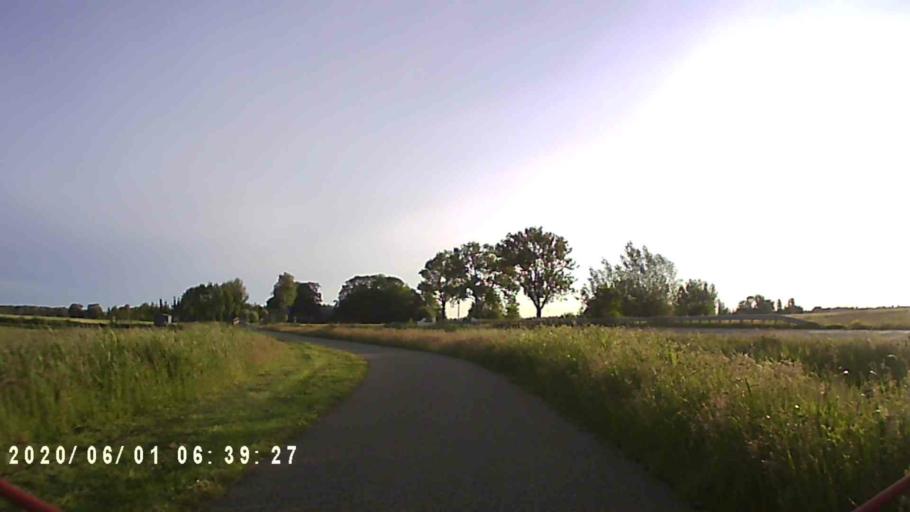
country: NL
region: Friesland
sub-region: Gemeente Kollumerland en Nieuwkruisland
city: Kollum
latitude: 53.2902
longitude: 6.1587
